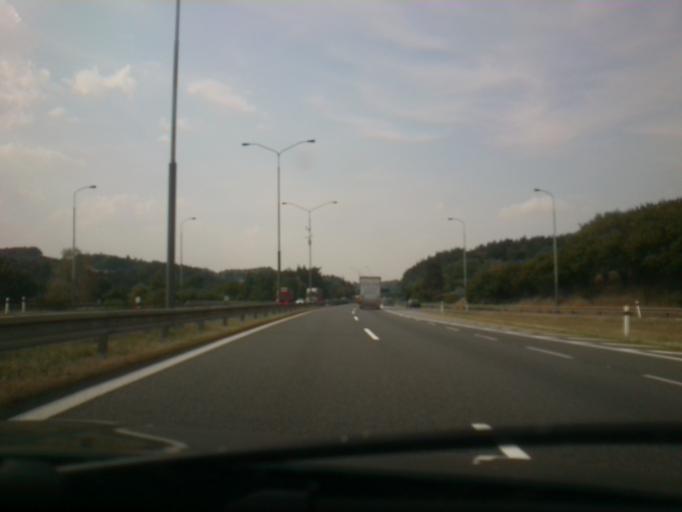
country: CZ
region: Central Bohemia
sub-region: Okres Praha-Vychod
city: Mnichovice
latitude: 49.9161
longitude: 14.7094
